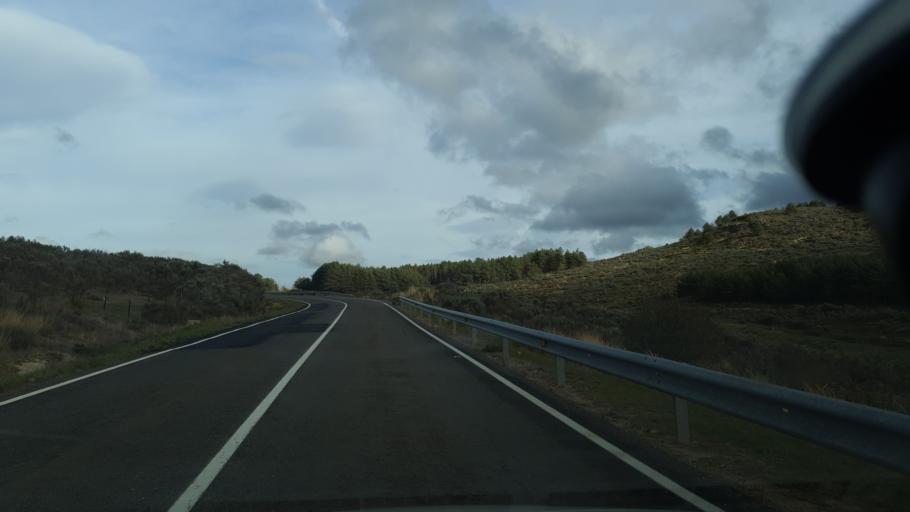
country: ES
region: Castille and Leon
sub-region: Provincia de Avila
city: Hoyocasero
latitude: 40.3892
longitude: -5.0041
